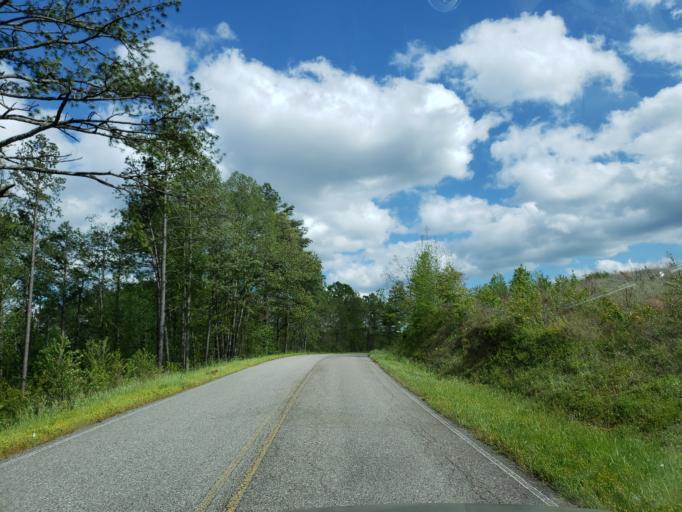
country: US
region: Georgia
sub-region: Haralson County
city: Tallapoosa
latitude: 33.7102
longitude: -85.3815
